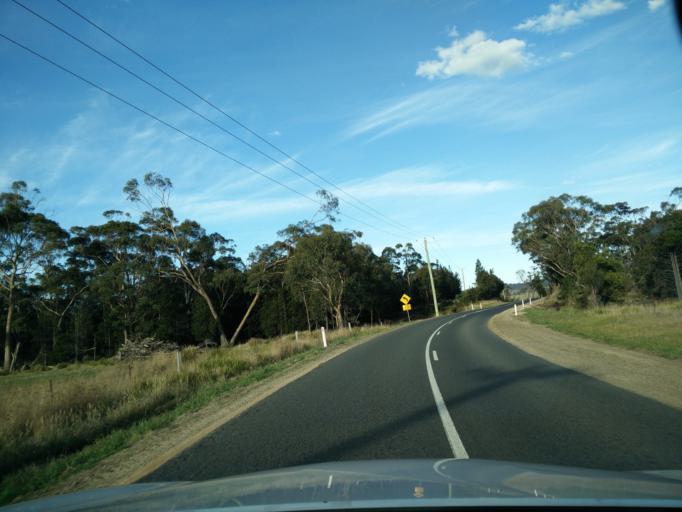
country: AU
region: Tasmania
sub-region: Break O'Day
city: St Helens
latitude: -41.9175
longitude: 148.2452
